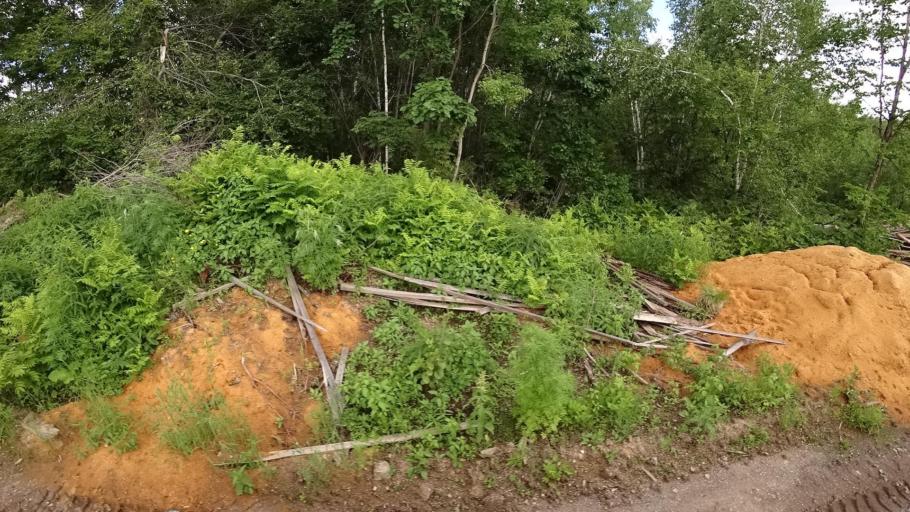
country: RU
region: Khabarovsk Krai
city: Litovko
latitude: 49.3590
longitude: 135.1776
